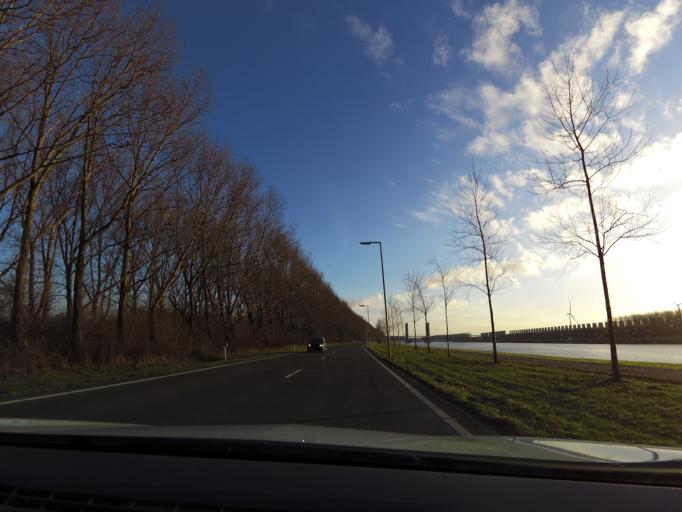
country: NL
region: South Holland
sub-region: Gemeente Maassluis
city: Maassluis
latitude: 51.9121
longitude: 4.2258
